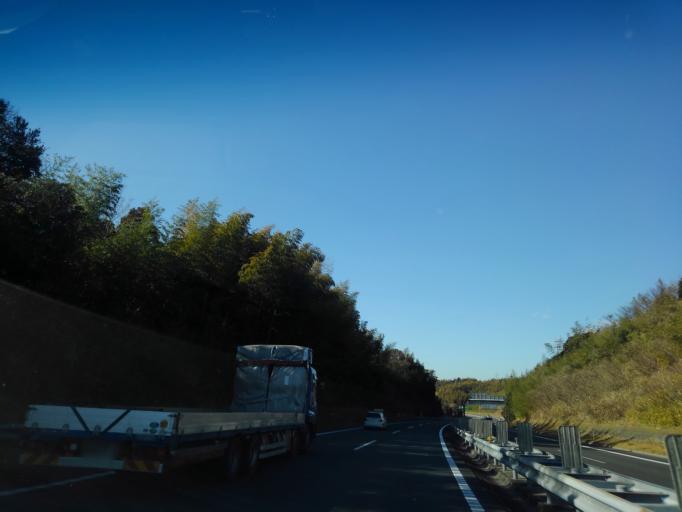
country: JP
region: Chiba
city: Kisarazu
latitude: 35.3531
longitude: 139.9414
